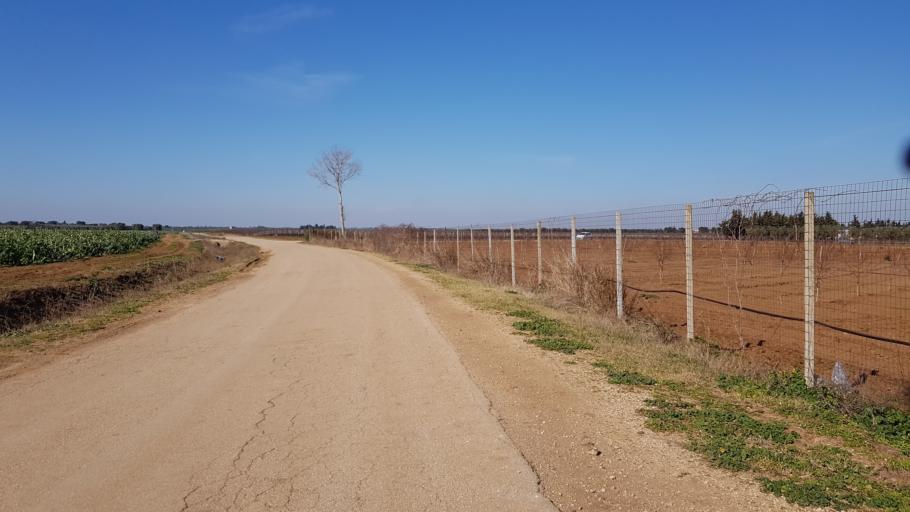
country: IT
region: Apulia
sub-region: Provincia di Brindisi
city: Mesagne
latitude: 40.6208
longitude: 17.8102
